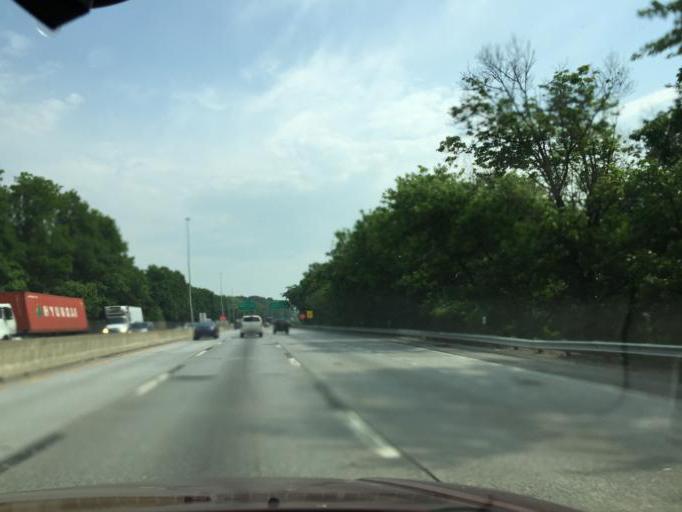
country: US
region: New York
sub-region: Westchester County
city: Mamaroneck
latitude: 40.9483
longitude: -73.7479
